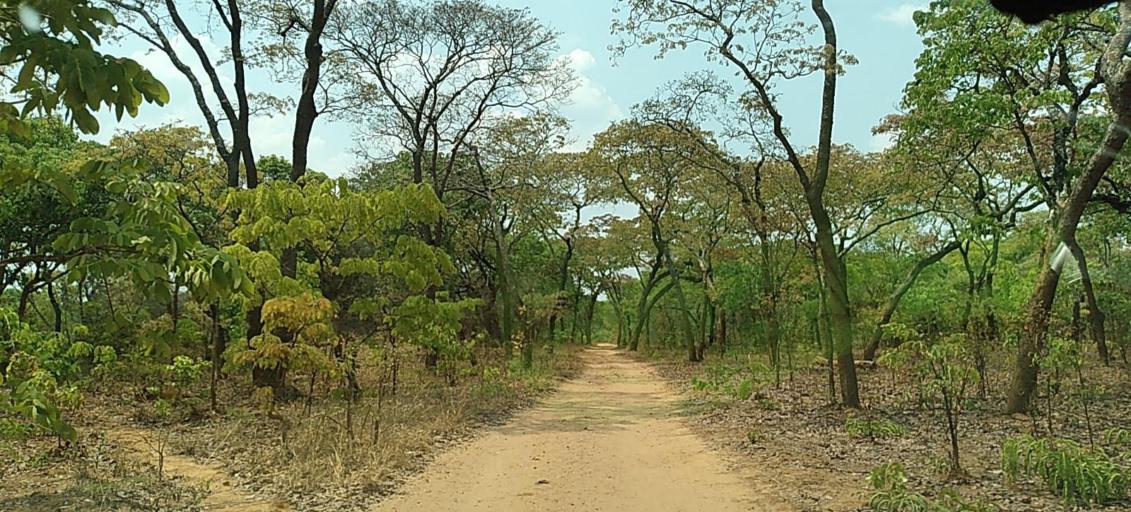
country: ZM
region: North-Western
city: Kabompo
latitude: -13.6488
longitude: 24.3758
